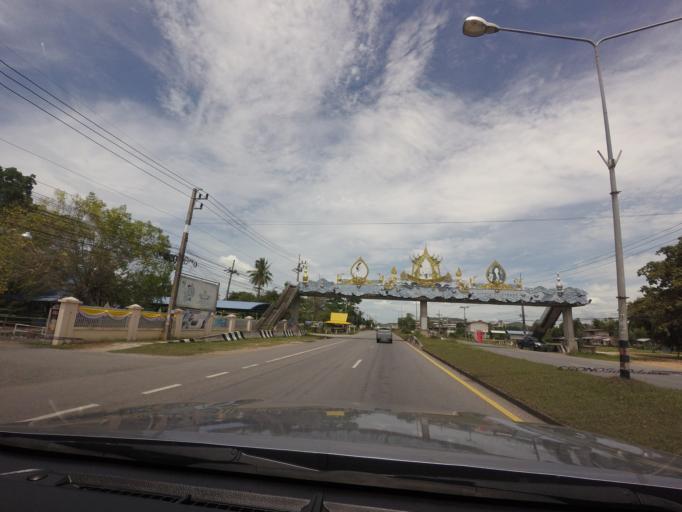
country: TH
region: Songkhla
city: Singhanakhon
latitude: 7.2404
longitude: 100.5481
